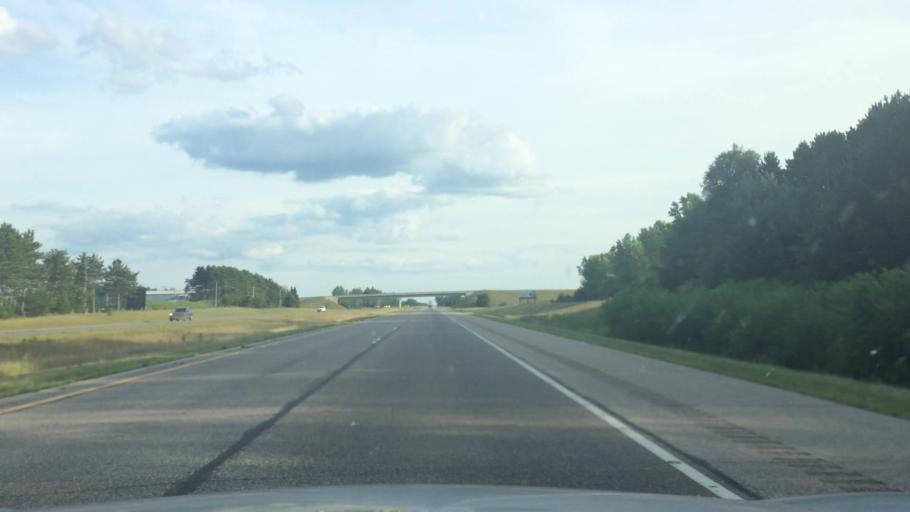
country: US
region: Wisconsin
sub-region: Portage County
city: Plover
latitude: 44.2918
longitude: -89.5237
